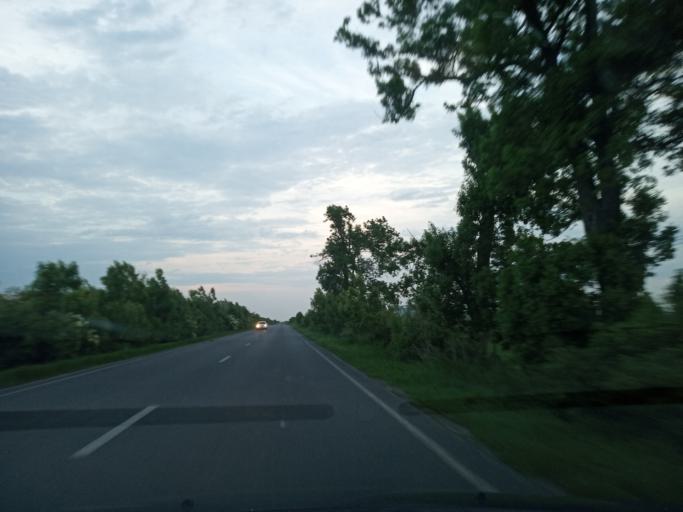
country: RO
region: Timis
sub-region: Comuna Voiteg
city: Voiteg
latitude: 45.4366
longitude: 21.2316
